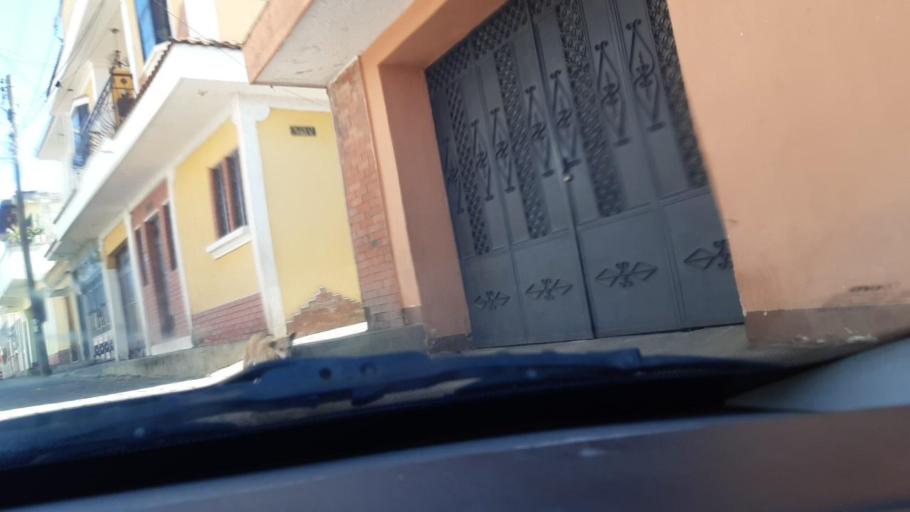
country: GT
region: Quetzaltenango
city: Salcaja
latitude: 14.8803
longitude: -91.4528
